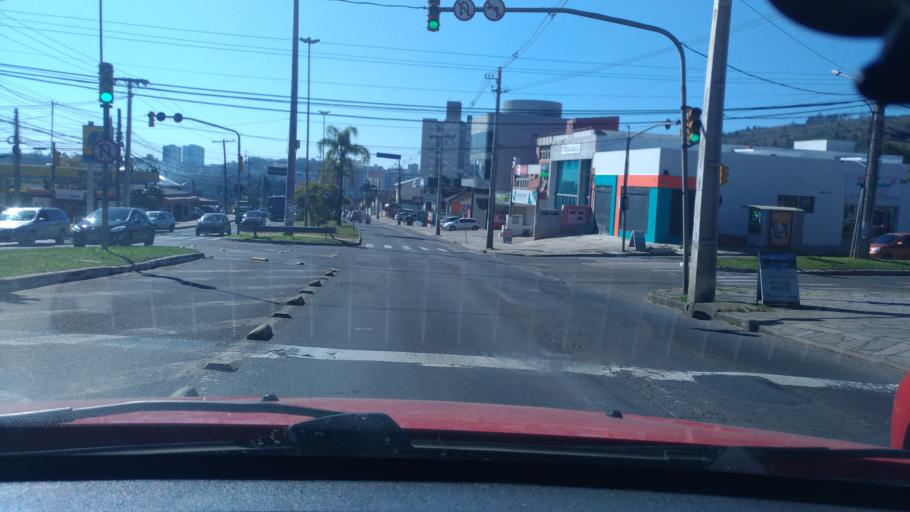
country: BR
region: Rio Grande do Sul
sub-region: Porto Alegre
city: Porto Alegre
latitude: -30.0427
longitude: -51.1361
